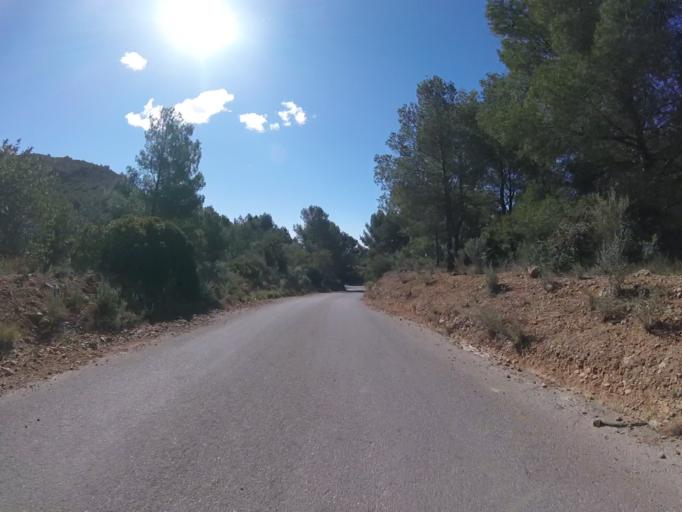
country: ES
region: Valencia
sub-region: Provincia de Castello
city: Benicassim
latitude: 40.0702
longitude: 0.0749
